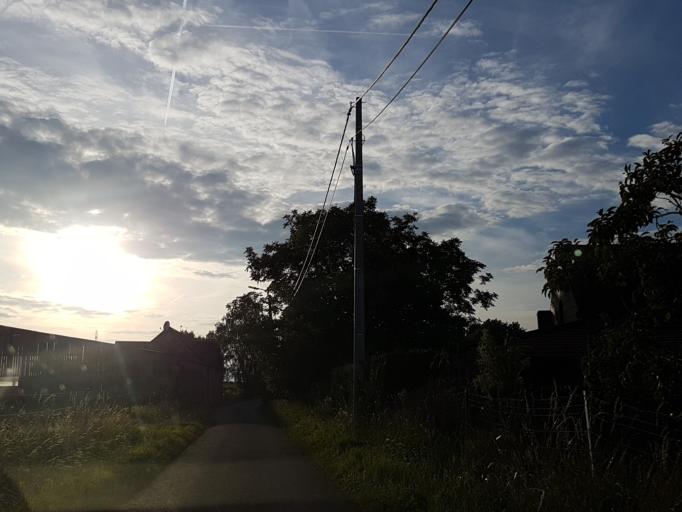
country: BE
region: Flanders
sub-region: Provincie Vlaams-Brabant
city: Merchtem
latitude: 50.9780
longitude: 4.2570
